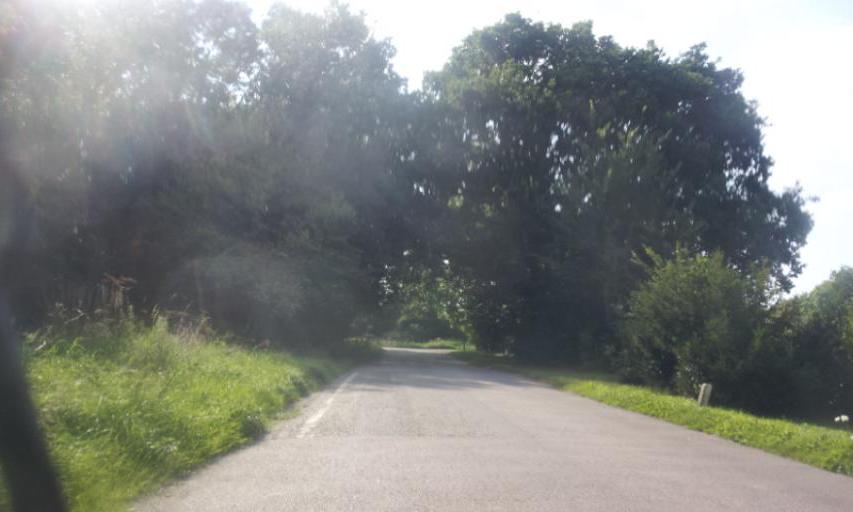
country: GB
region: England
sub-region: Kent
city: Yalding
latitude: 51.1999
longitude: 0.4413
